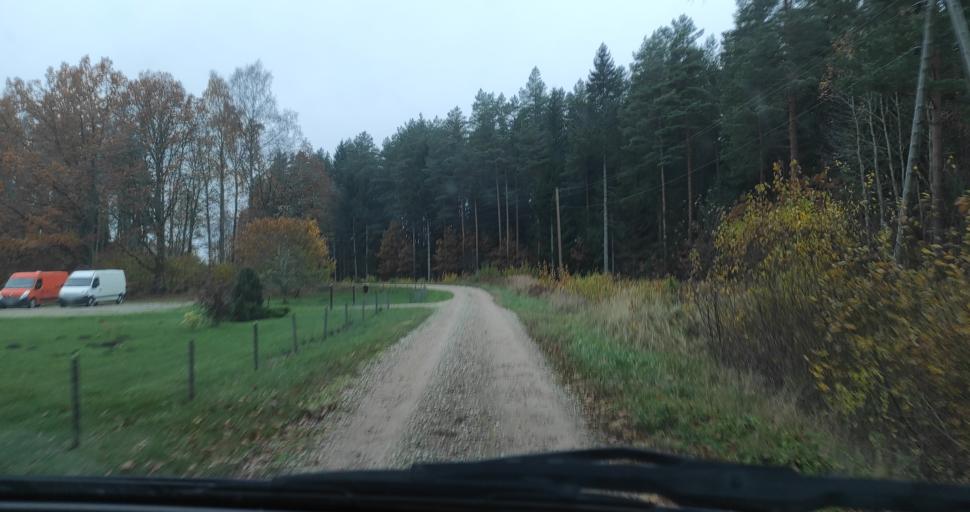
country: LV
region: Durbe
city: Liegi
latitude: 56.7503
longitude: 21.3442
